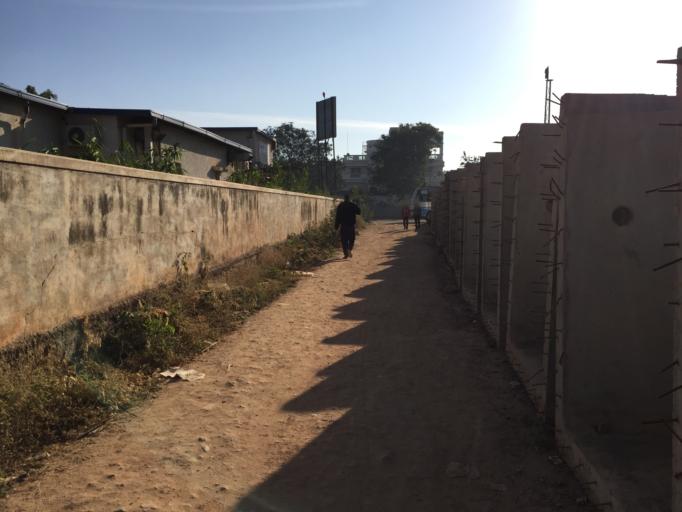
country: IN
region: Karnataka
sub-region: Bangalore Urban
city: Yelahanka
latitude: 13.0541
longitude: 77.6191
